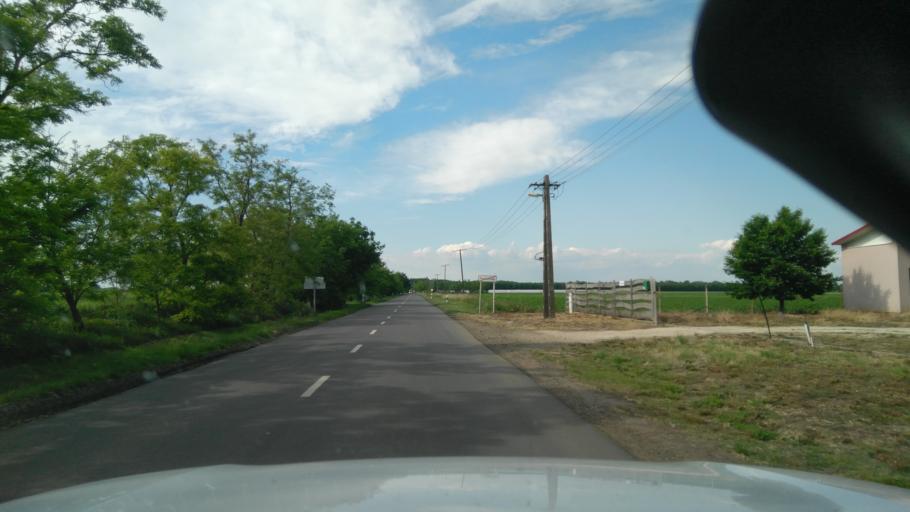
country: HU
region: Bekes
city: Ujkigyos
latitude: 46.5491
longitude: 20.9754
